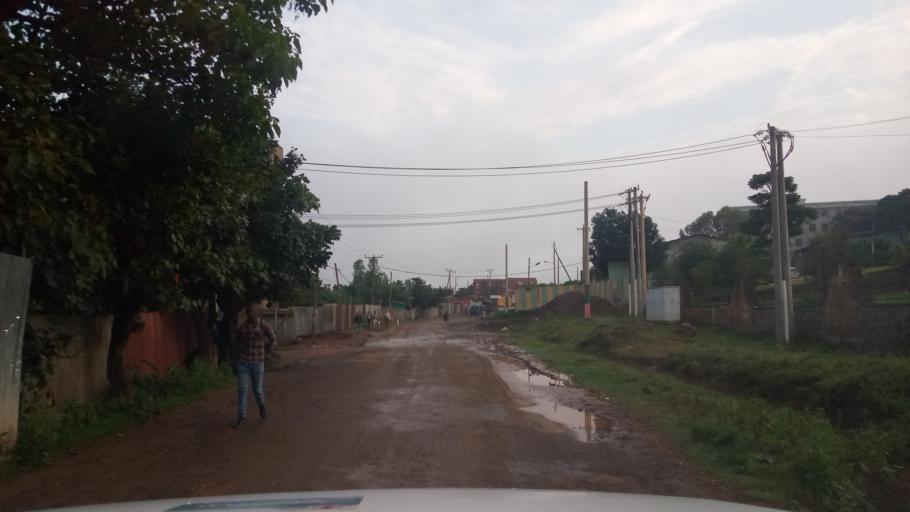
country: ET
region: Oromiya
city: Jima
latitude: 7.6812
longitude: 36.8504
